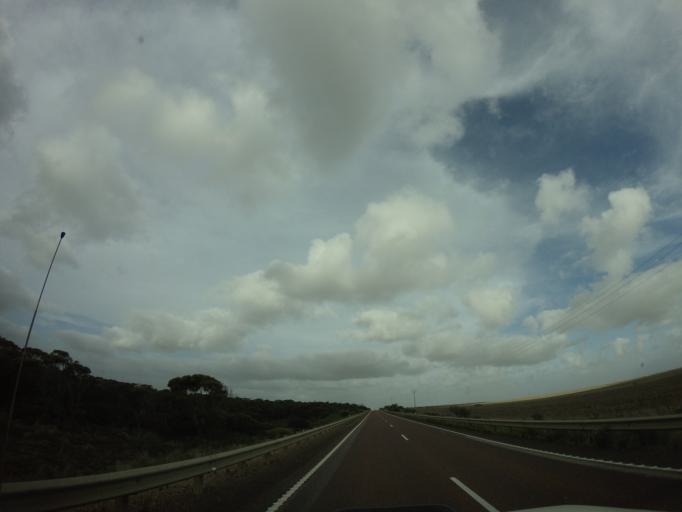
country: AU
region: South Australia
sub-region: Ceduna
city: Ceduna
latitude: -32.0662
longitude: 133.6384
